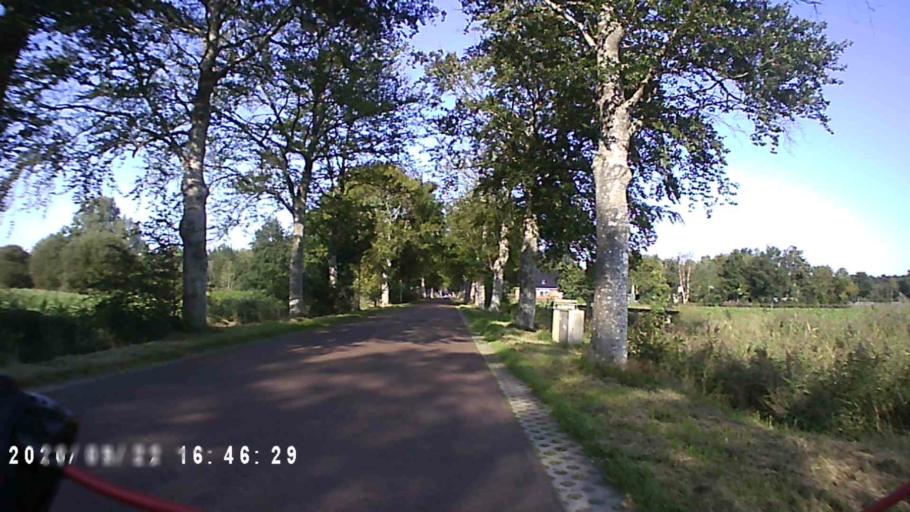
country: NL
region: Groningen
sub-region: Gemeente Leek
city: Leek
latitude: 53.1295
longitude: 6.4714
